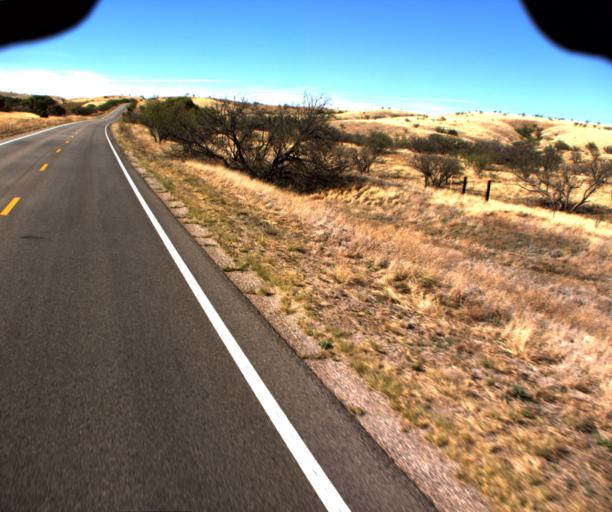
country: US
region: Arizona
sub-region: Pima County
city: Corona de Tucson
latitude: 31.7889
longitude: -110.6985
